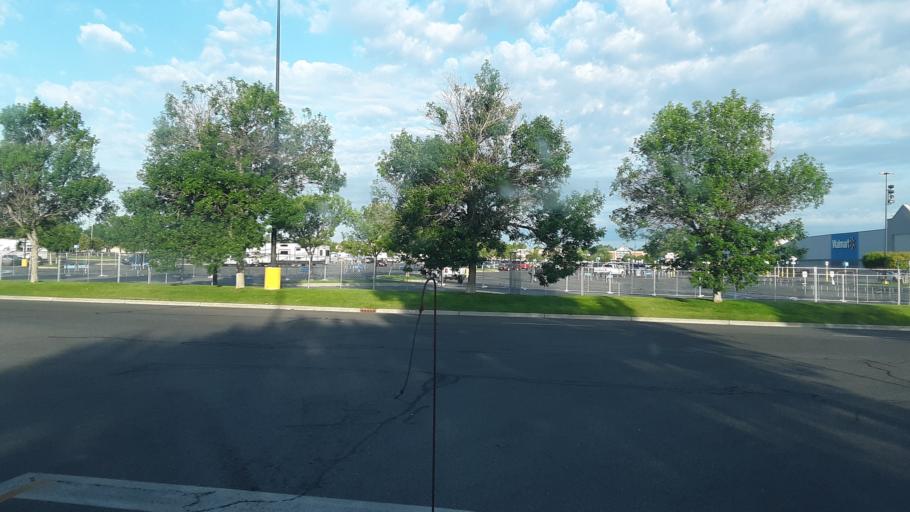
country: US
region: Montana
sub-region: Yellowstone County
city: Billings
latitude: 45.7571
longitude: -108.5776
